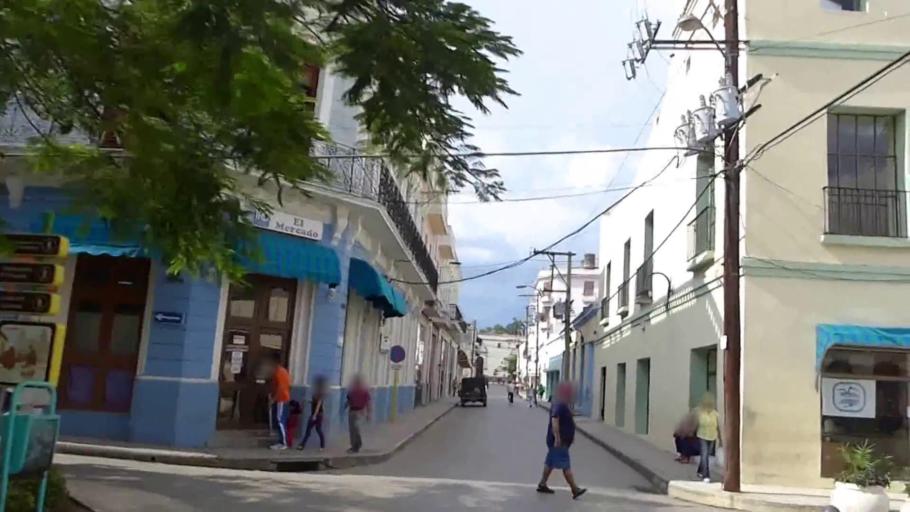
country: CU
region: Camaguey
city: Camaguey
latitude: 21.3810
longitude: -77.9182
